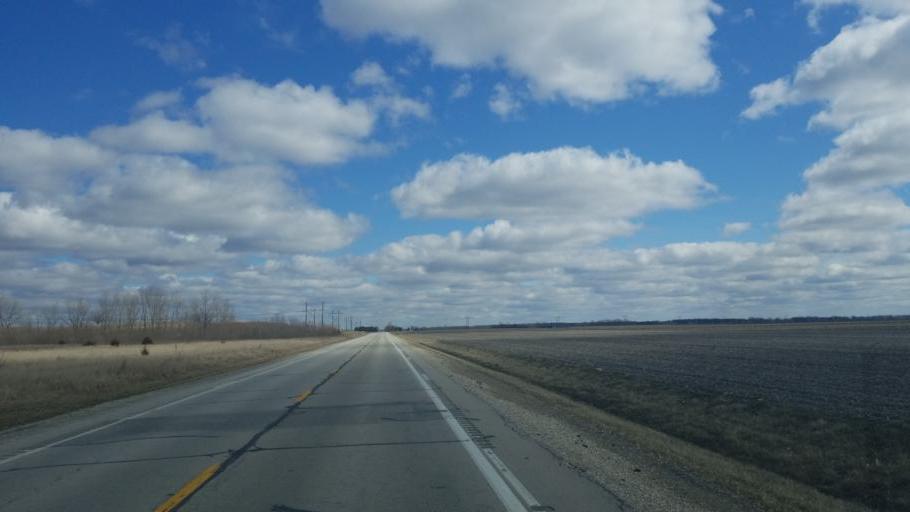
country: US
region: Illinois
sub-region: Douglas County
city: Villa Grove
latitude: 39.7922
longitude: -88.0588
